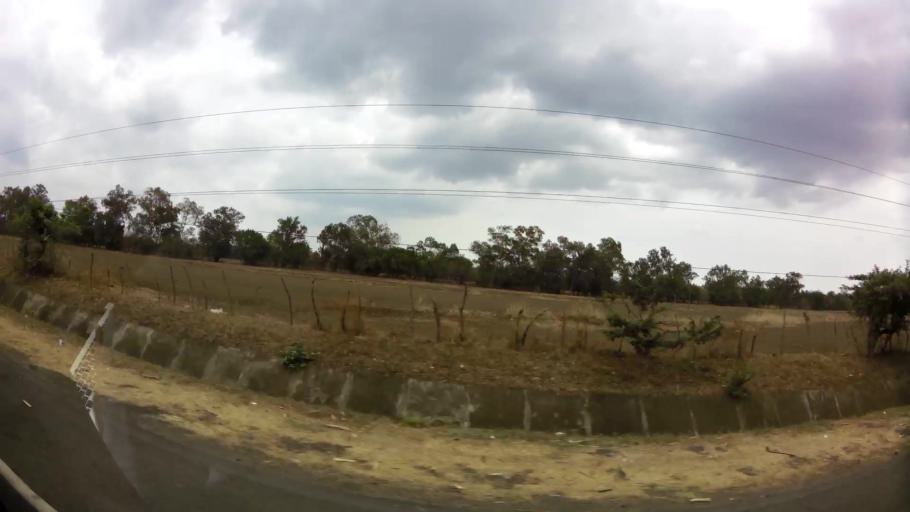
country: NI
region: Leon
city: Telica
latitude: 12.4835
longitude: -86.8618
